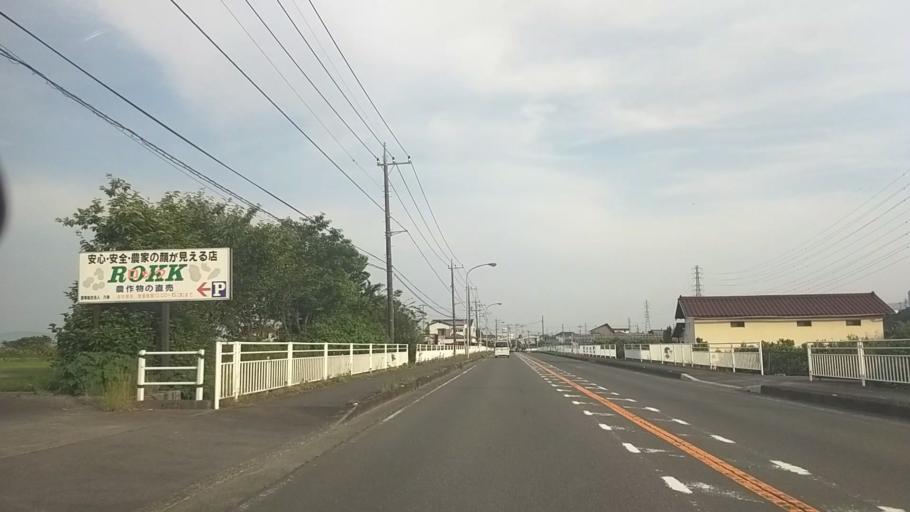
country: JP
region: Kanagawa
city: Odawara
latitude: 35.3393
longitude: 139.1035
